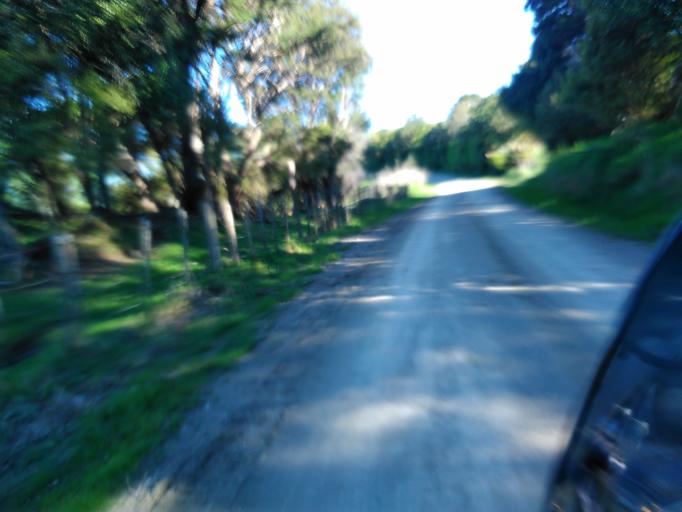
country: NZ
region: Gisborne
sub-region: Gisborne District
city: Gisborne
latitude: -38.3974
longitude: 177.6760
